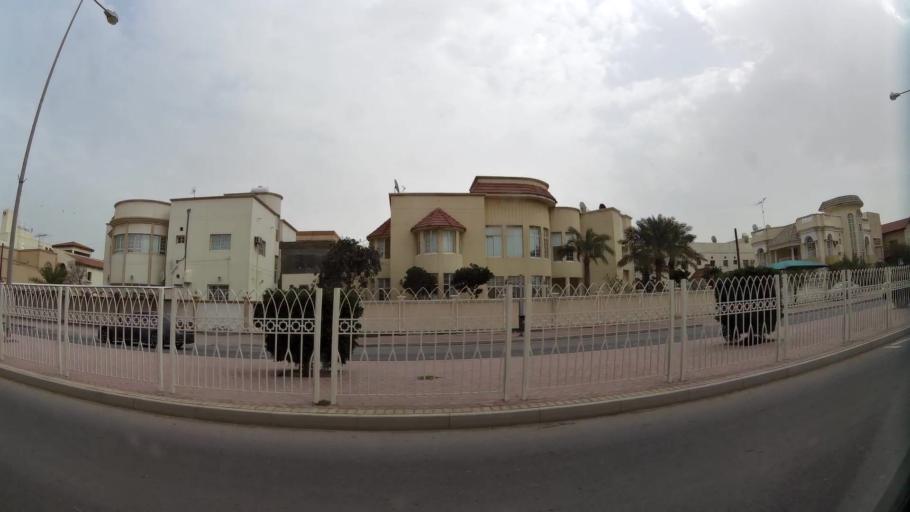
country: BH
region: Northern
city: Ar Rifa'
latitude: 26.1287
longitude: 50.5610
